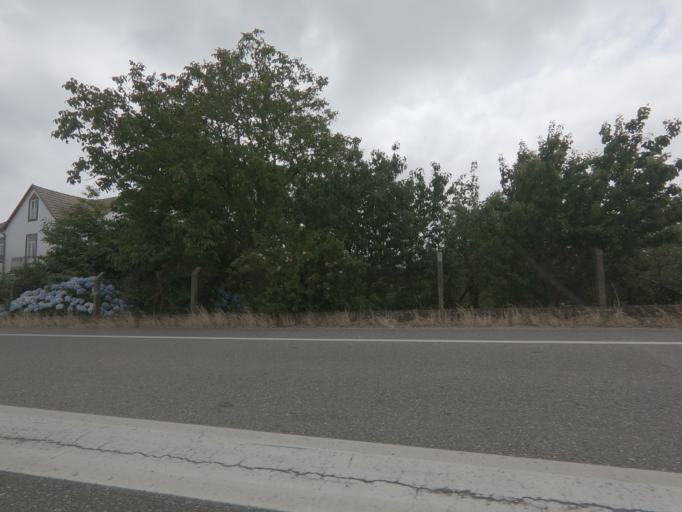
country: ES
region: Galicia
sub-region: Provincia de Pontevedra
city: O Rosal
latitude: 41.9246
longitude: -8.8063
